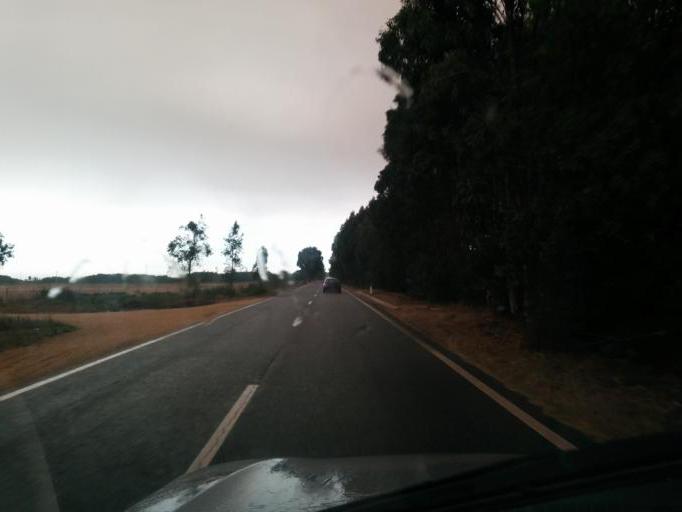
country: PT
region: Beja
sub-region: Odemira
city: Vila Nova de Milfontes
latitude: 37.6867
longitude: -8.7654
